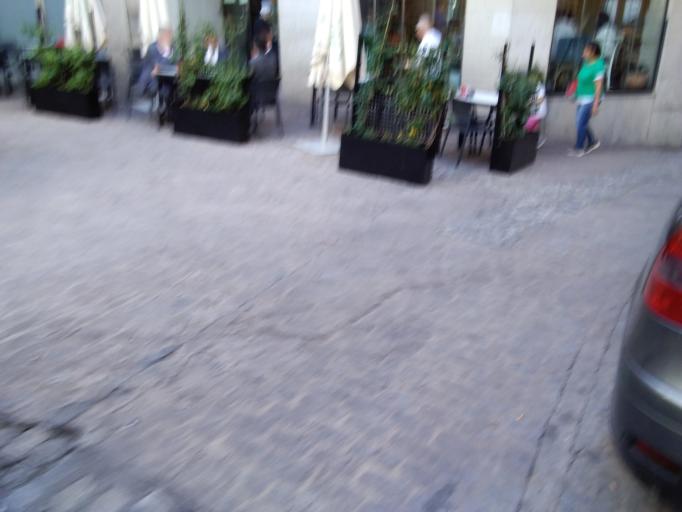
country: ES
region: Castille-La Mancha
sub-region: Province of Toledo
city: Toledo
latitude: 39.8596
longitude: -4.0226
